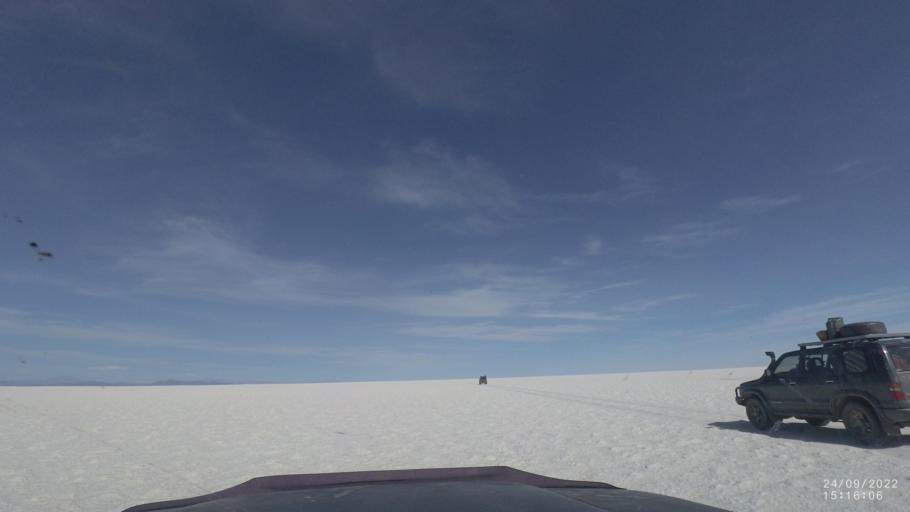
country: BO
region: Potosi
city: Colchani
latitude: -19.9790
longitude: -67.4386
